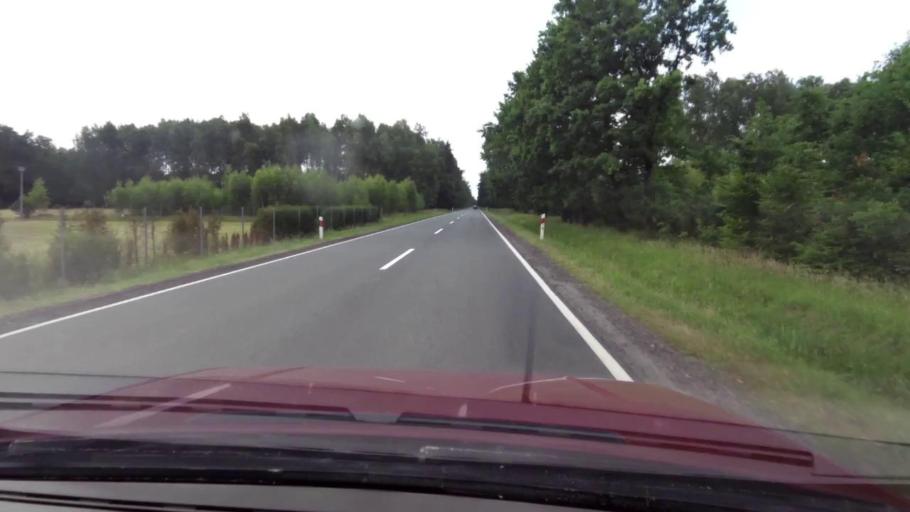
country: PL
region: Pomeranian Voivodeship
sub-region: Powiat bytowski
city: Trzebielino
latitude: 54.2179
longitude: 17.0885
